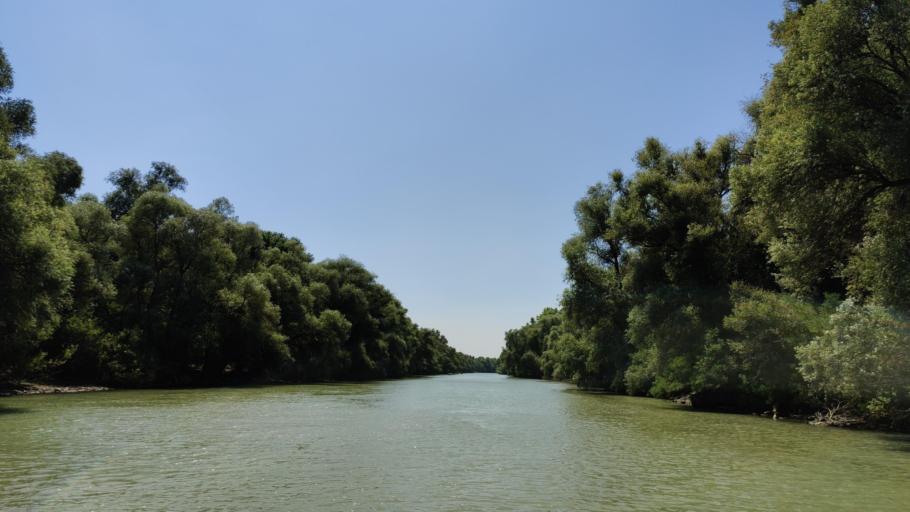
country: RO
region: Tulcea
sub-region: Comuna Pardina
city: Pardina
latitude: 45.2448
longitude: 28.9217
